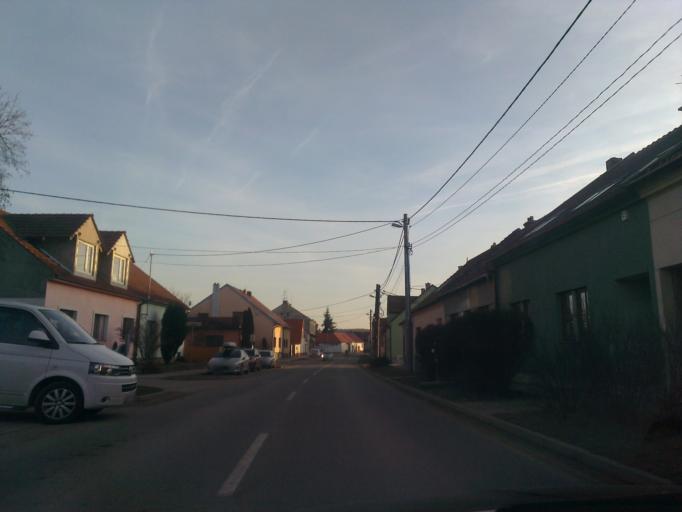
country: CZ
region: South Moravian
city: Bilovice nad Svitavou
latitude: 49.2570
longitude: 16.7320
